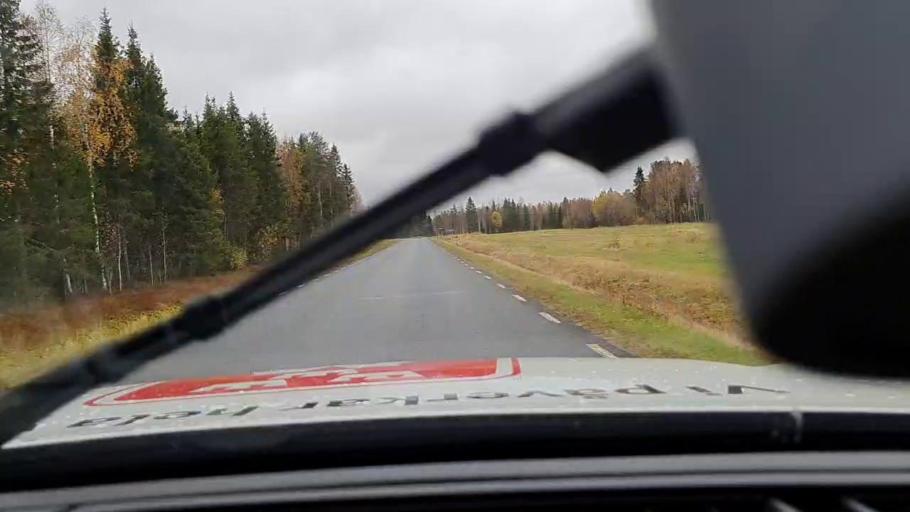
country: SE
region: Norrbotten
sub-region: Haparanda Kommun
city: Haparanda
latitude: 65.9308
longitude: 23.8164
